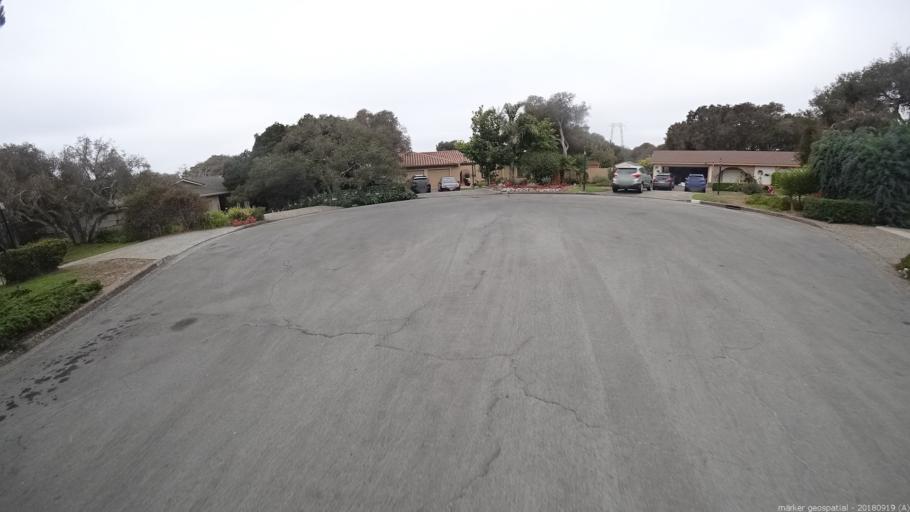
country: US
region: California
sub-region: Monterey County
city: Prunedale
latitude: 36.7824
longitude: -121.7132
